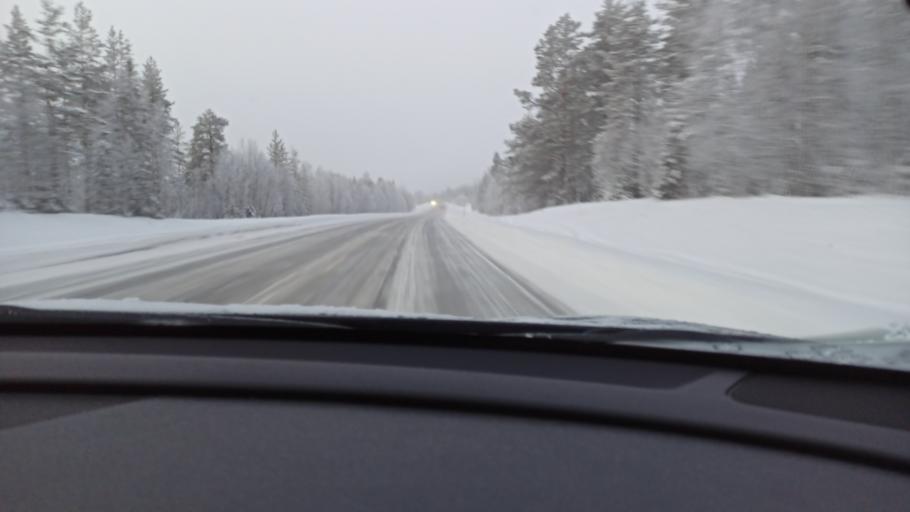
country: FI
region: Lapland
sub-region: Pohjois-Lappi
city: Sodankylae
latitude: 66.9293
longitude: 26.2464
